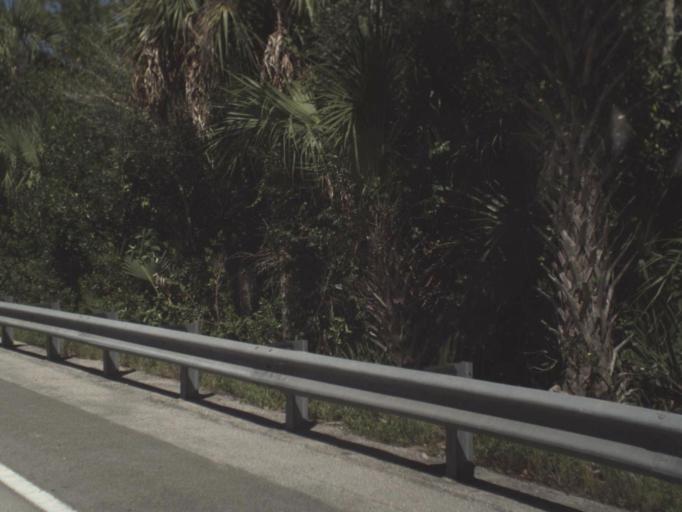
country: US
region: Florida
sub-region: Collier County
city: Marco
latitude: 25.9655
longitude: -81.5288
